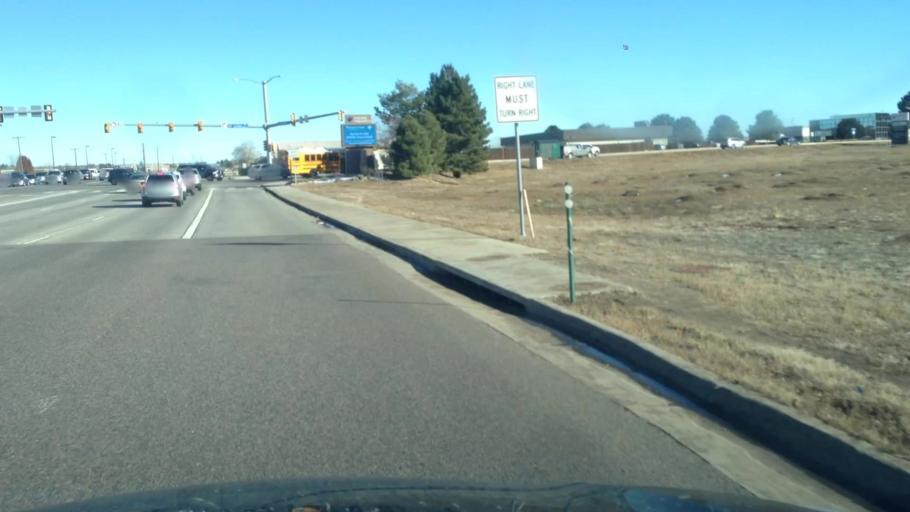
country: US
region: Colorado
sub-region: Arapahoe County
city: Dove Valley
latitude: 39.5948
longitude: -104.8224
